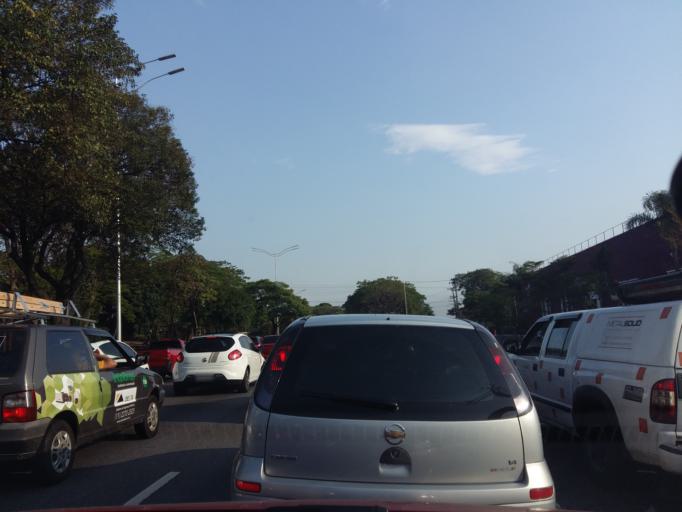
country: BR
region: Sao Paulo
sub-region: Diadema
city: Diadema
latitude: -23.6286
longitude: -46.6481
